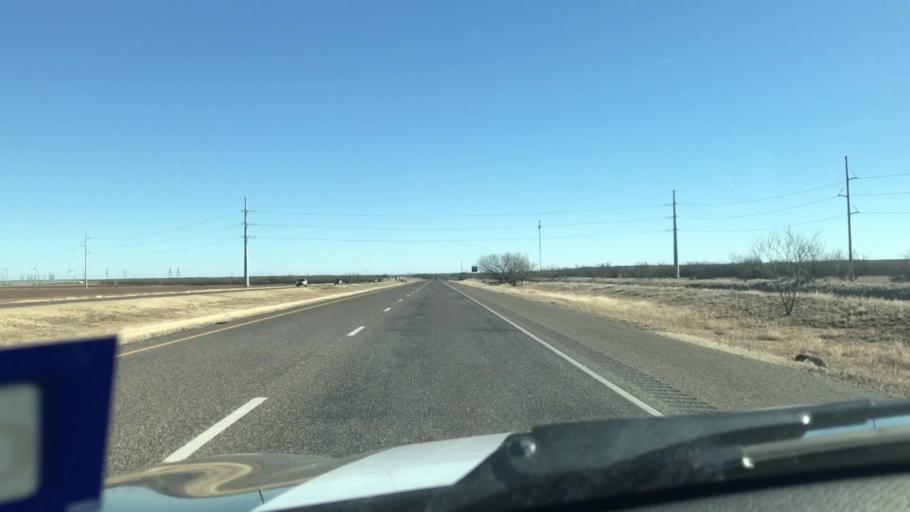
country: US
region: Texas
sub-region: Scurry County
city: Snyder
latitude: 32.8665
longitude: -101.0330
